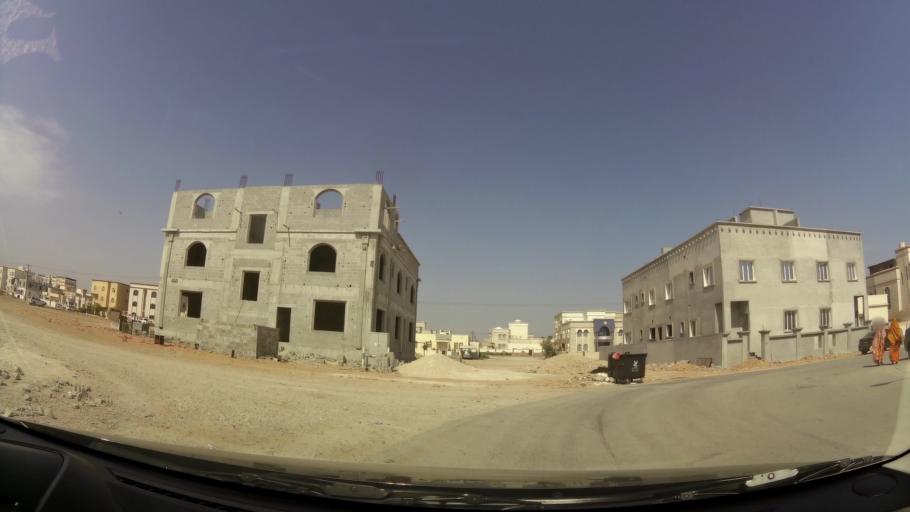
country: OM
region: Zufar
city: Salalah
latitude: 17.0472
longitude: 54.1538
